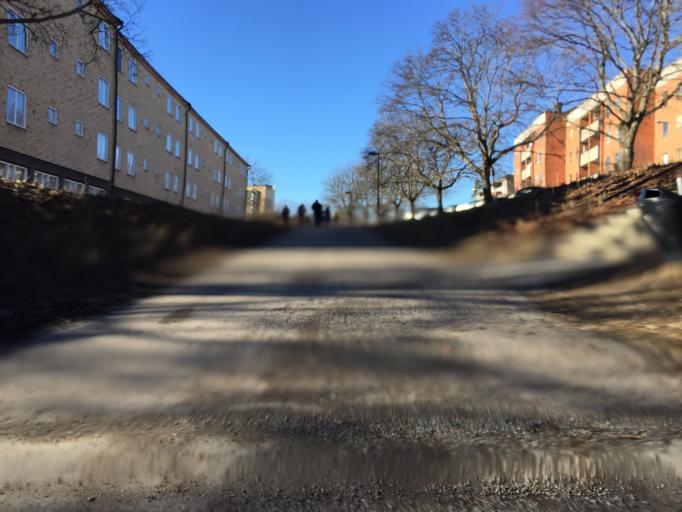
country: SE
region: Stockholm
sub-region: Stockholms Kommun
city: Bromma
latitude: 59.3640
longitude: 17.8788
